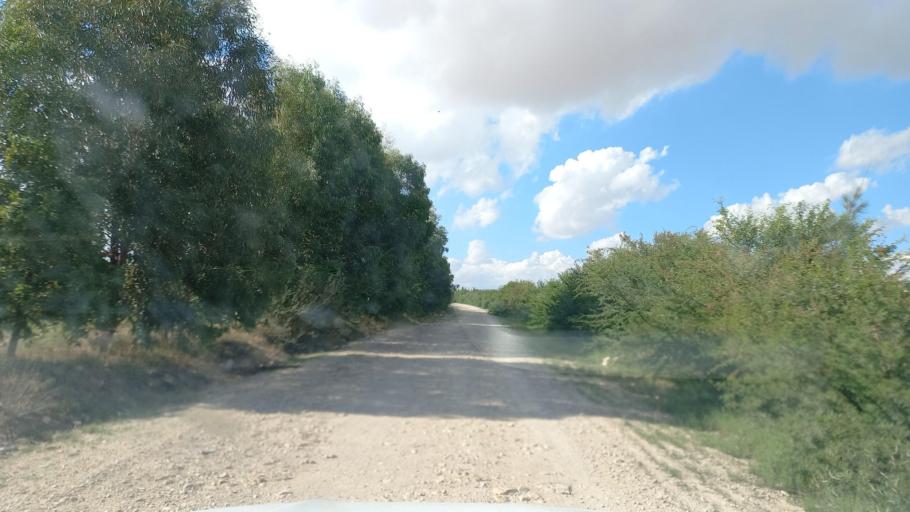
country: TN
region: Al Qasrayn
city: Sbiba
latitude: 35.3379
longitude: 9.0785
